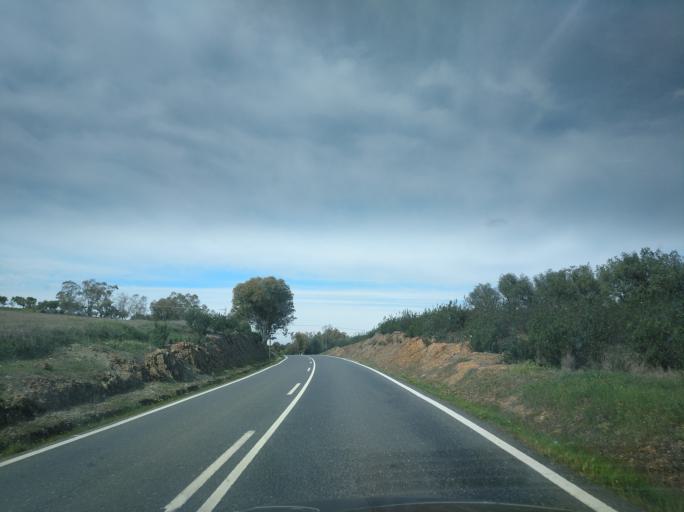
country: PT
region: Beja
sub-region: Mertola
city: Mertola
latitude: 37.7203
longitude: -7.7604
